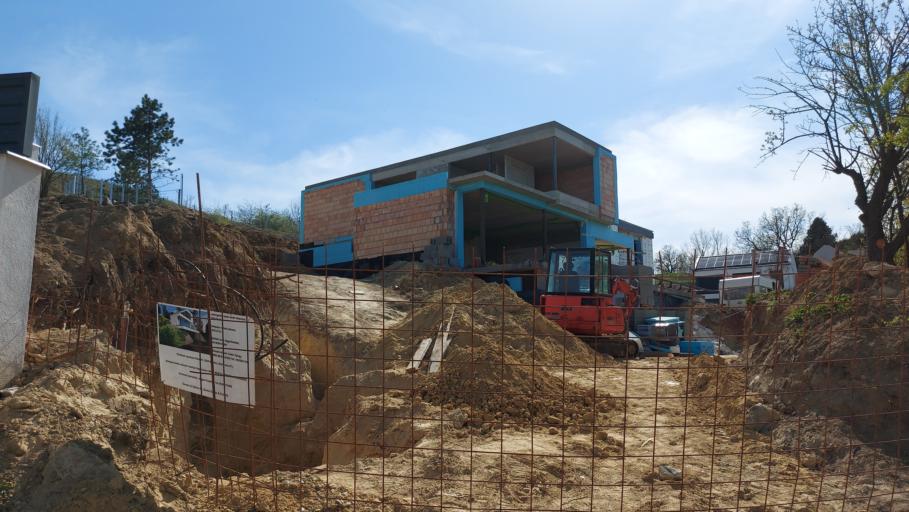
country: HU
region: Pest
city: Budaors
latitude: 47.4333
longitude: 18.9703
